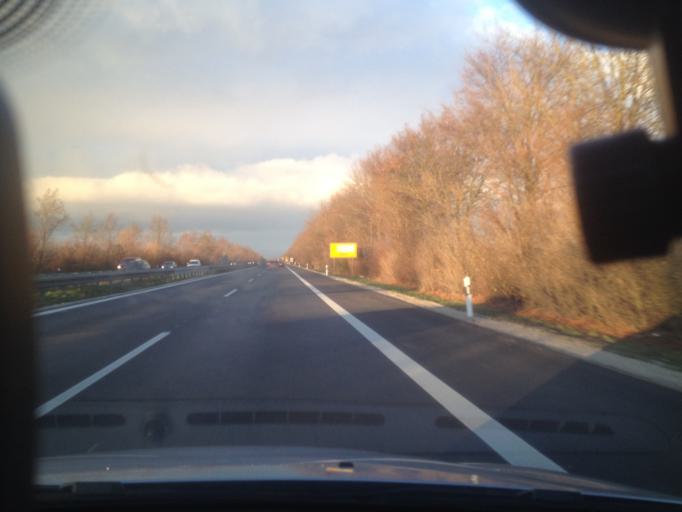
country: DE
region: Bavaria
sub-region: Swabia
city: Konigsbrunn
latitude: 48.2992
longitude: 10.8791
